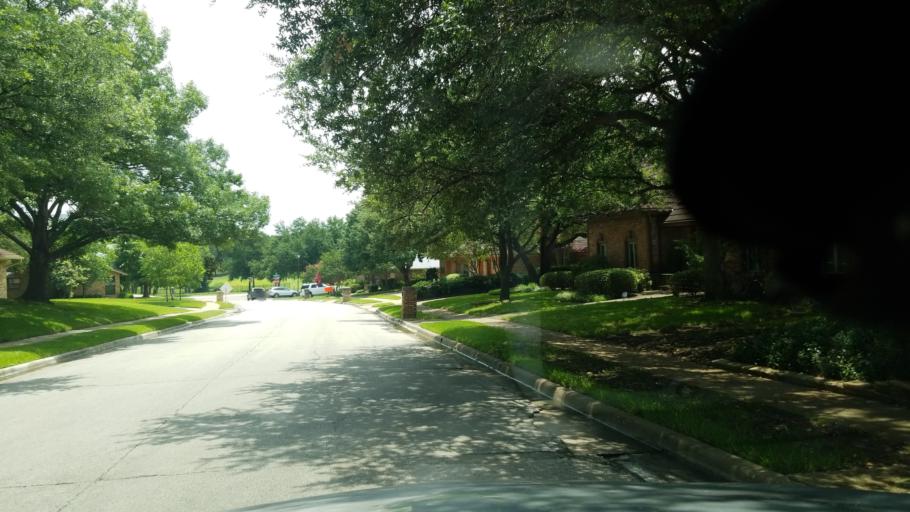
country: US
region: Texas
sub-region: Dallas County
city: Irving
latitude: 32.8535
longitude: -96.9354
